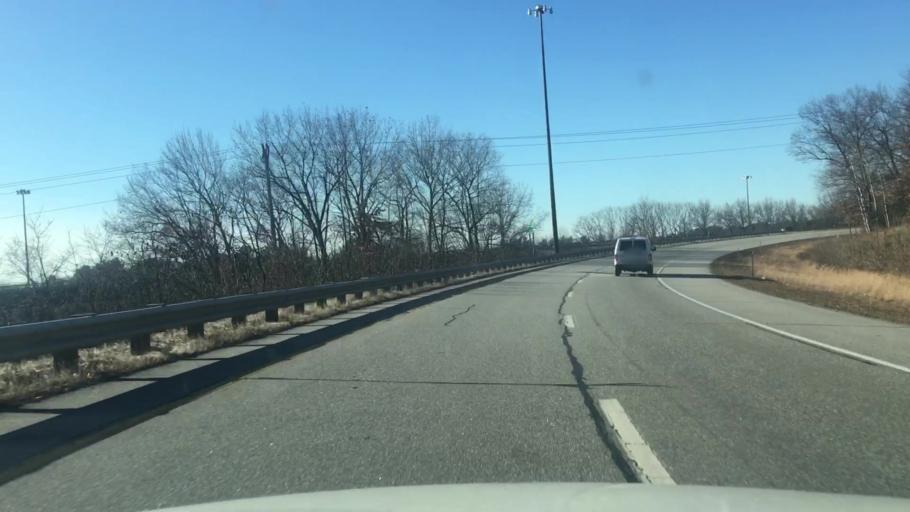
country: US
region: New Hampshire
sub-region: Merrimack County
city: South Hooksett
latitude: 42.9966
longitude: -71.4159
